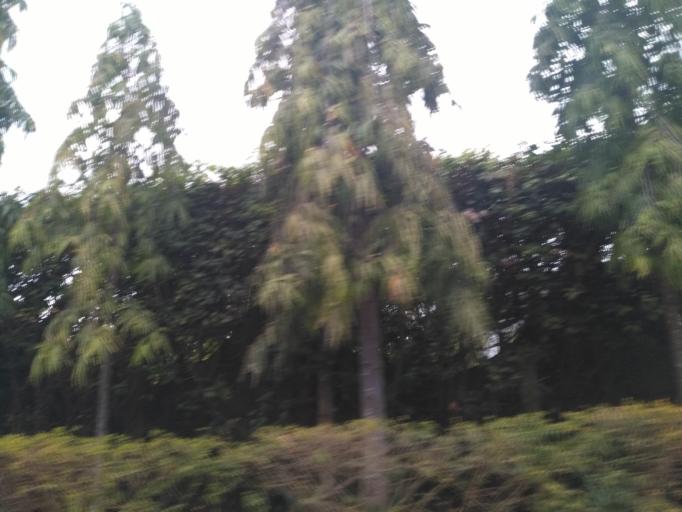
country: TZ
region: Dar es Salaam
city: Magomeni
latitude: -6.7700
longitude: 39.2723
